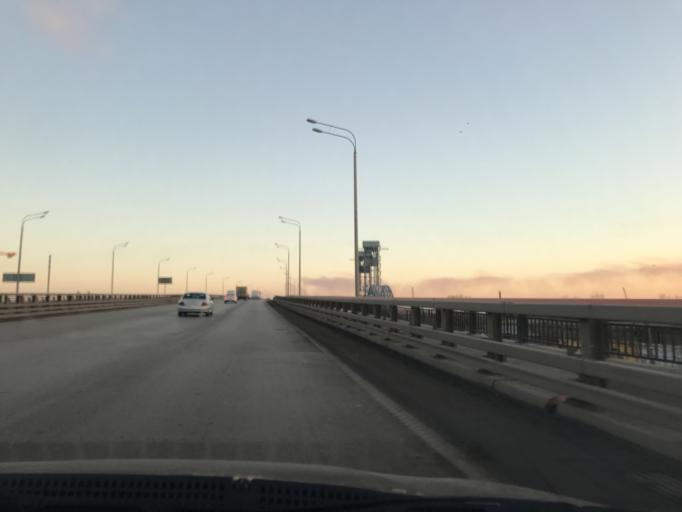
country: RU
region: Rostov
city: Rostov-na-Donu
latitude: 47.2139
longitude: 39.6993
